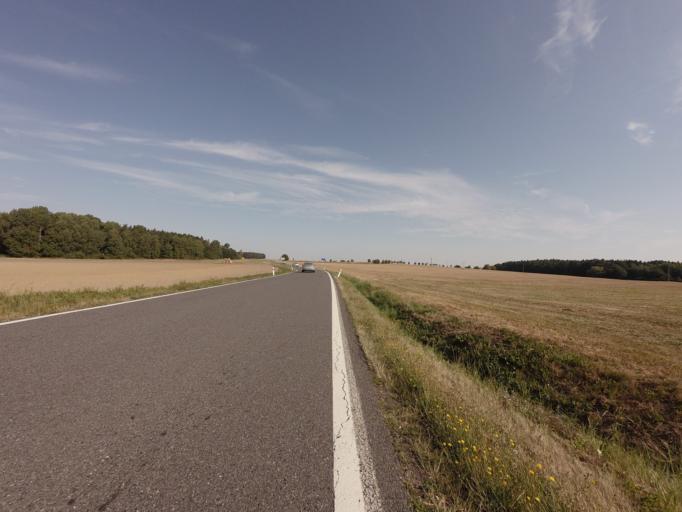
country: CZ
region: Jihocesky
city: Bernartice
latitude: 49.3152
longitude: 14.3724
